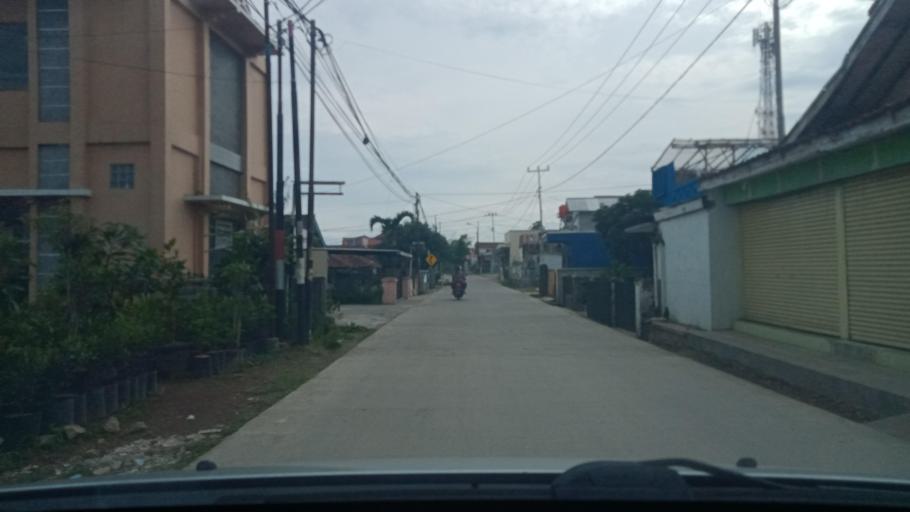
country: ID
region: West Java
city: Lembang
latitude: -6.8080
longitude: 107.5870
